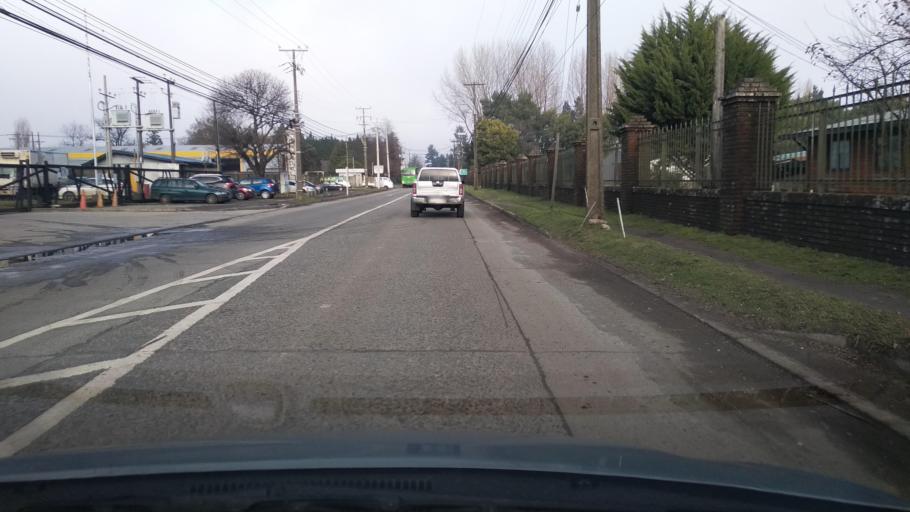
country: CL
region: Los Rios
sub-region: Provincia de Valdivia
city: Valdivia
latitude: -39.8093
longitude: -73.2339
